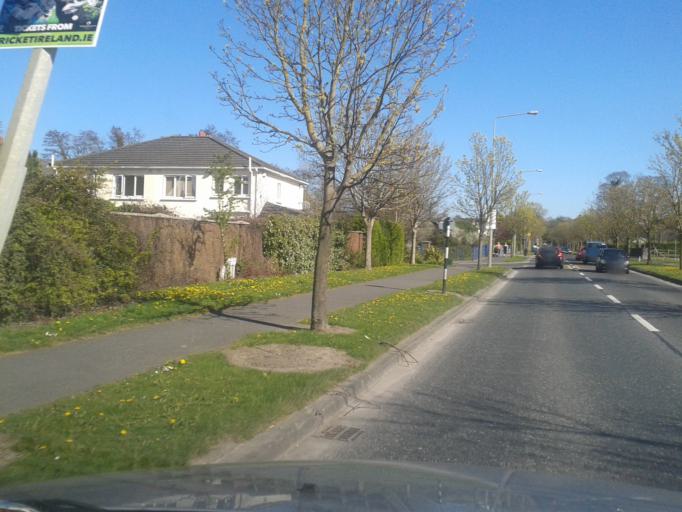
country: IE
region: Leinster
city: Kinsealy-Drinan
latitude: 53.4488
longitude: -6.1813
